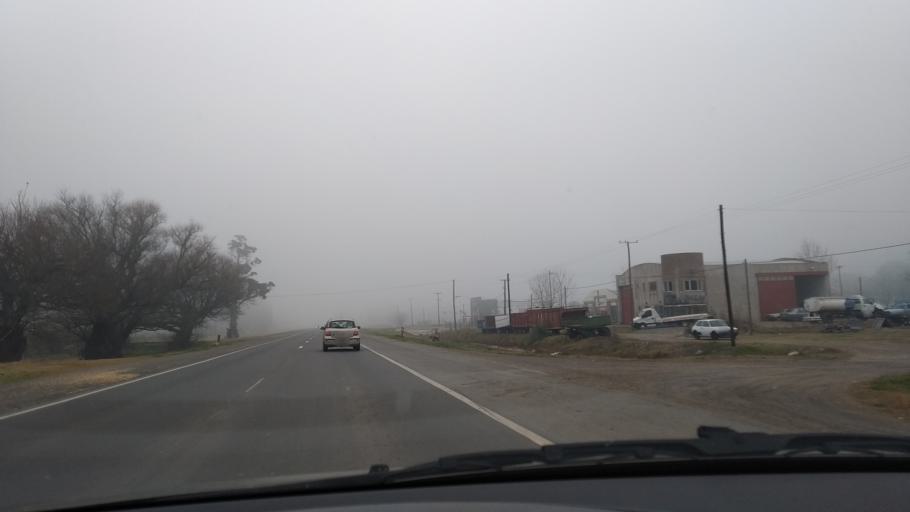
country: AR
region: Buenos Aires
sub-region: Partido de Azul
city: Azul
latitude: -36.8069
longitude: -59.8581
